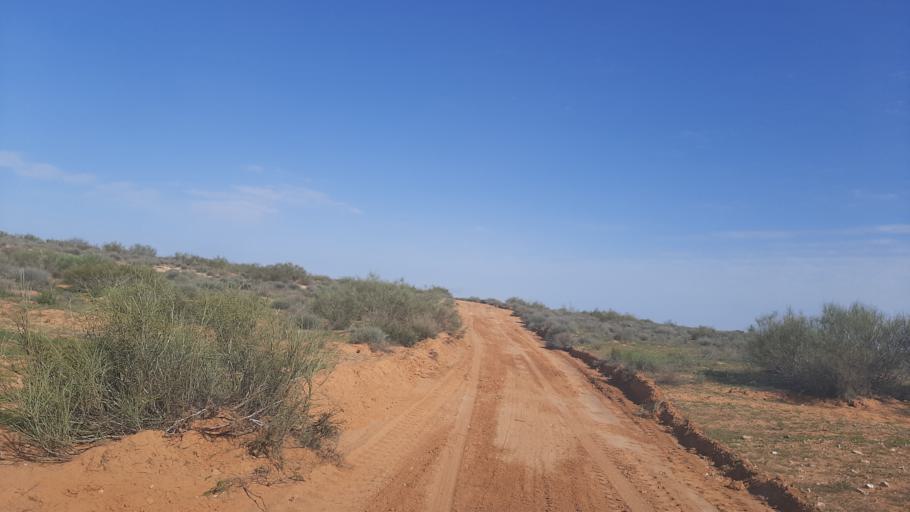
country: TN
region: Madanin
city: Medenine
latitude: 33.2441
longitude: 10.7419
